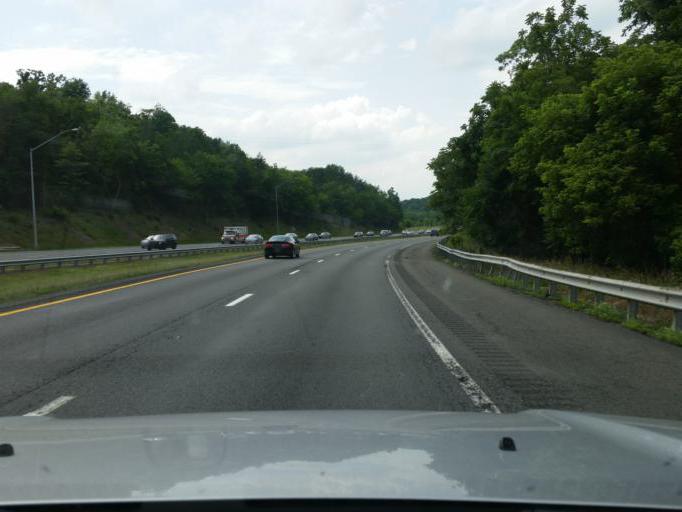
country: US
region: Maryland
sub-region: Frederick County
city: Green Valley
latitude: 39.2741
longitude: -77.3192
